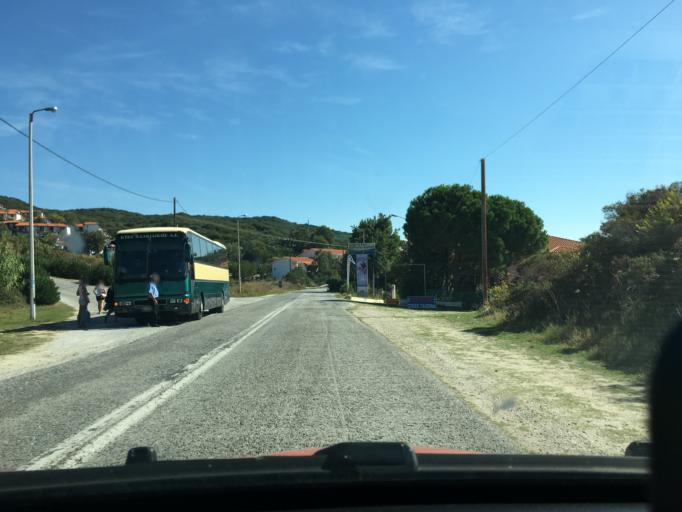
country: GR
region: Central Macedonia
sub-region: Nomos Chalkidikis
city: Ouranoupolis
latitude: 40.3492
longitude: 23.9602
